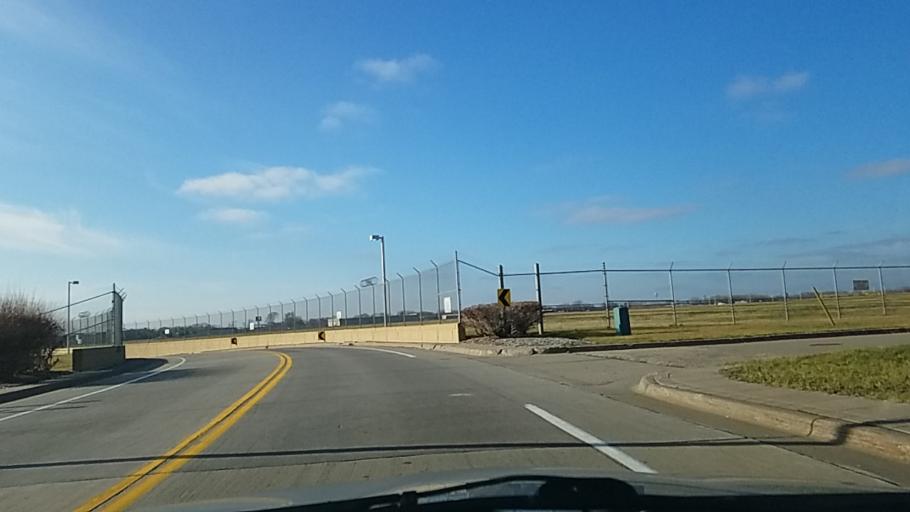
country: US
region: Minnesota
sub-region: Hennepin County
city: Richfield
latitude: 44.8846
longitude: -93.2348
